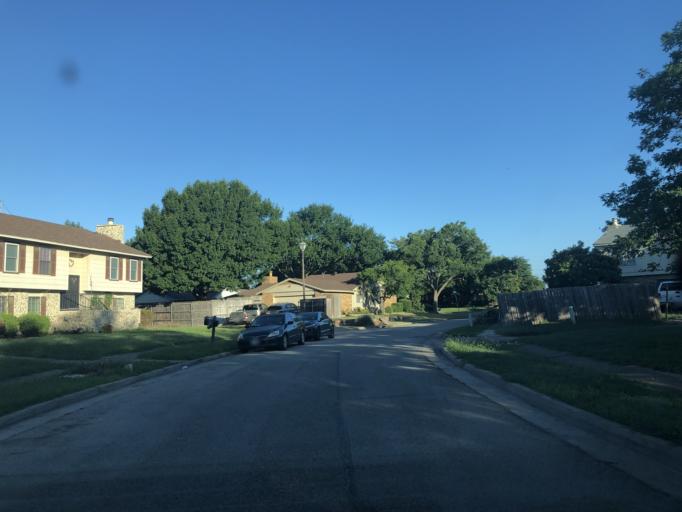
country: US
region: Texas
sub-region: Dallas County
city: Duncanville
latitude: 32.6458
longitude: -96.9501
